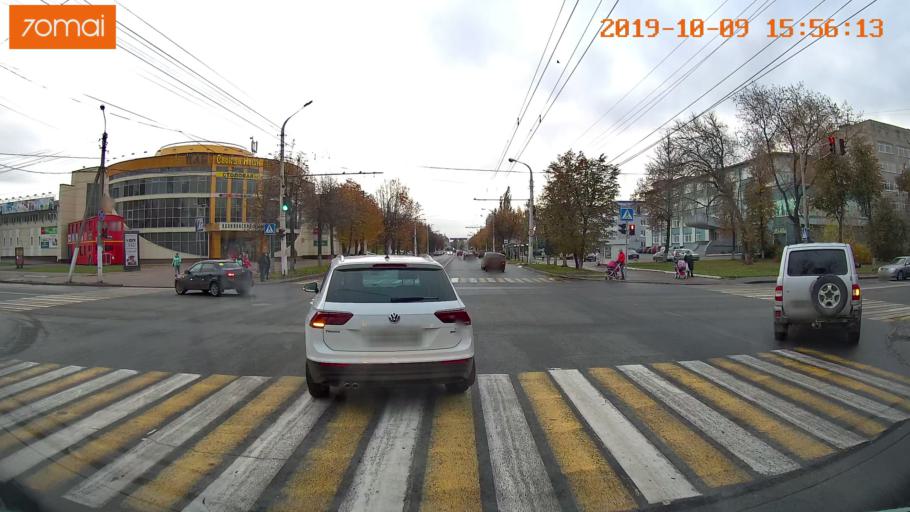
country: RU
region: Kostroma
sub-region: Kostromskoy Rayon
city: Kostroma
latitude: 57.7755
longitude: 40.9442
